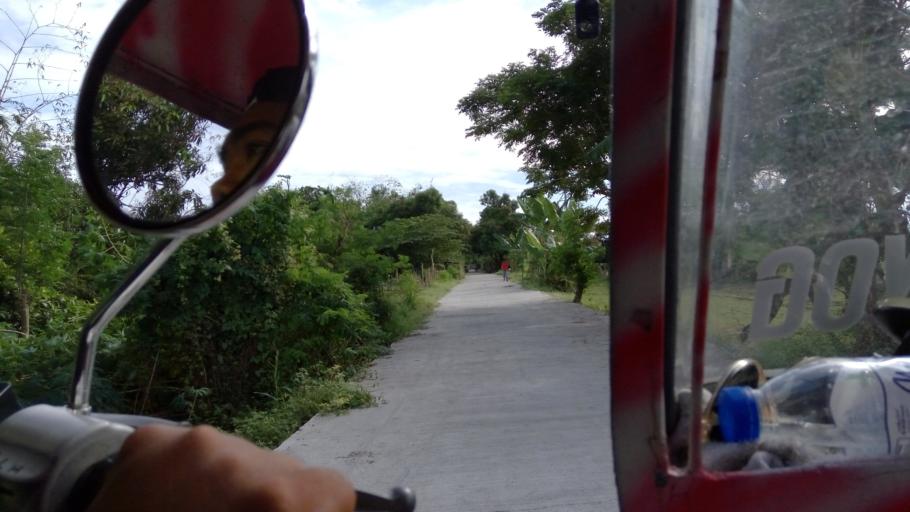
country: PH
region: Ilocos
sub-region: Province of La Union
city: San Eugenio
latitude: 16.3626
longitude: 120.3525
